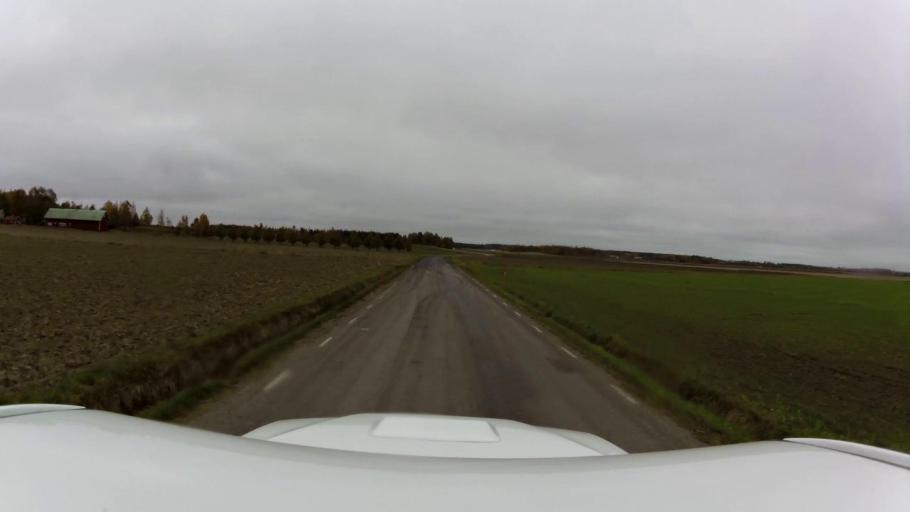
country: SE
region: OEstergoetland
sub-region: Linkopings Kommun
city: Linghem
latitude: 58.4480
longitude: 15.7111
